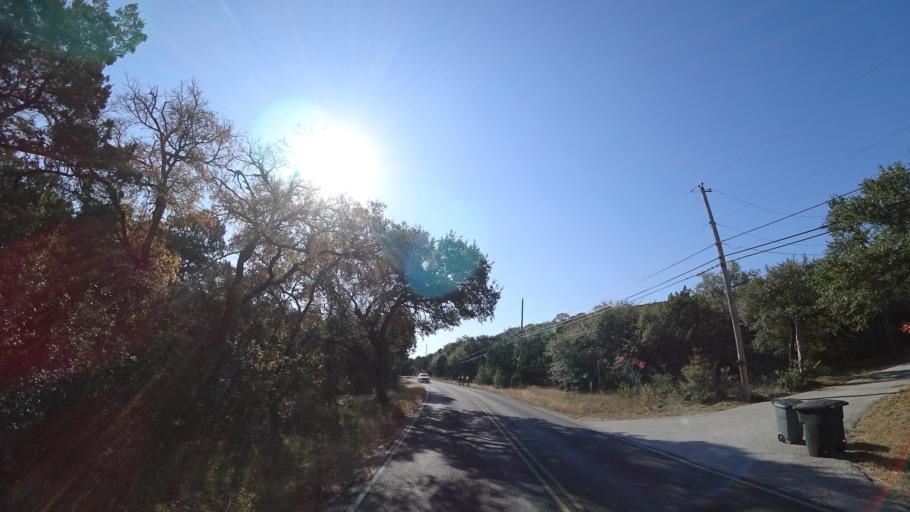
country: US
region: Texas
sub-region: Williamson County
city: Jollyville
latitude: 30.3892
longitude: -97.7741
